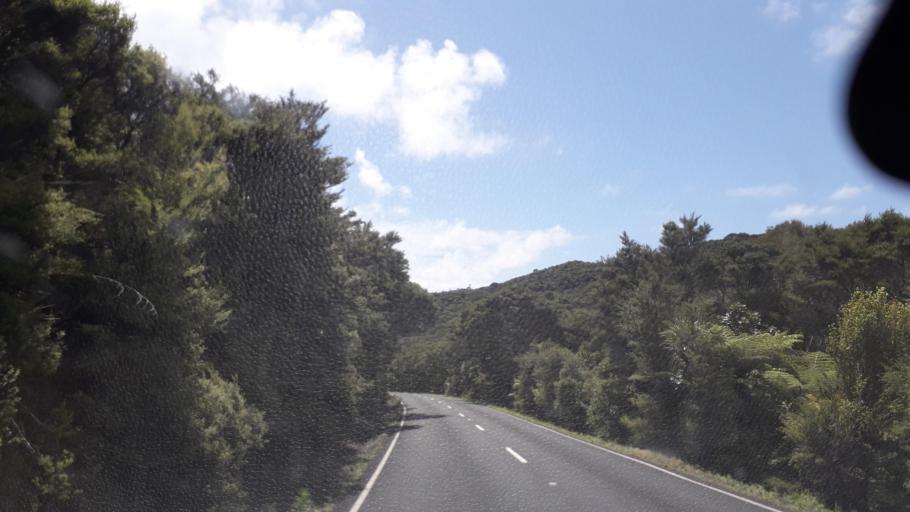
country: NZ
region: Northland
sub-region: Far North District
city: Paihia
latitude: -35.2503
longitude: 174.2603
